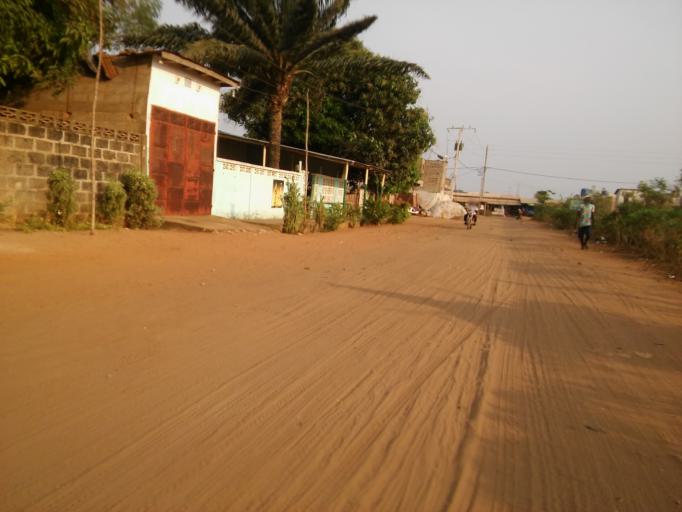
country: BJ
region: Atlantique
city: Abomey-Calavi
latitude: 6.4184
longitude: 2.3343
